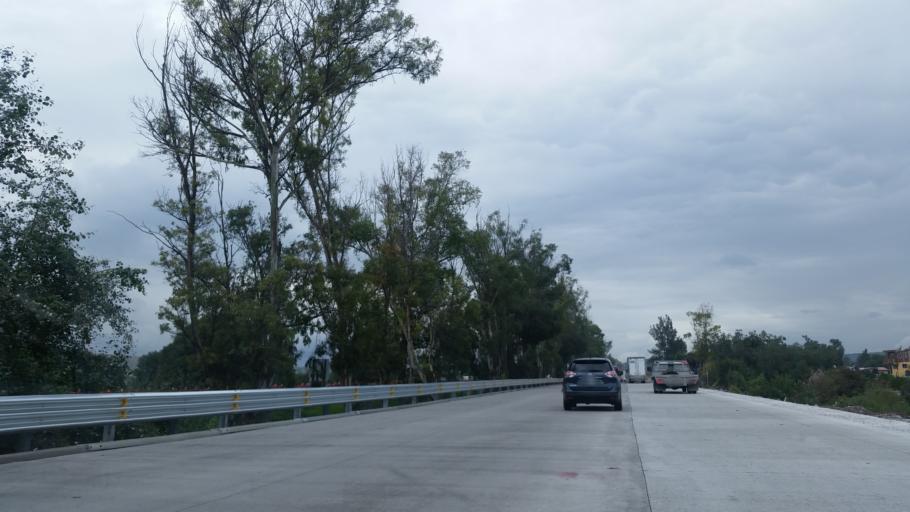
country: MX
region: Mexico
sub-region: Huehuetoca
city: Villa URBI del Rey
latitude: 19.8363
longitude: -99.2729
